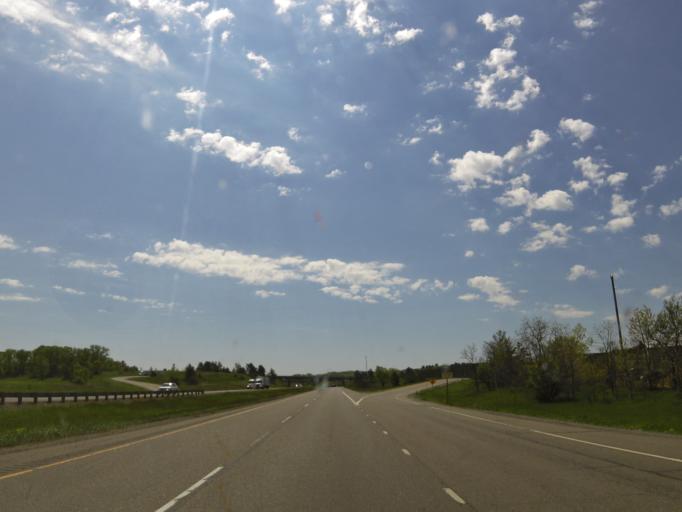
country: US
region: Wisconsin
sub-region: Trempealeau County
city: Osseo
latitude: 44.4620
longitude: -91.0954
